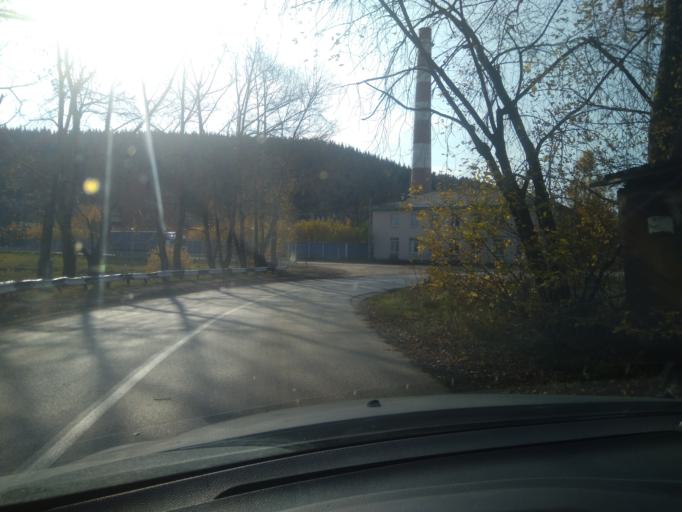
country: RU
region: Sverdlovsk
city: Nizhniye Sergi
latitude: 56.6691
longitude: 59.3196
